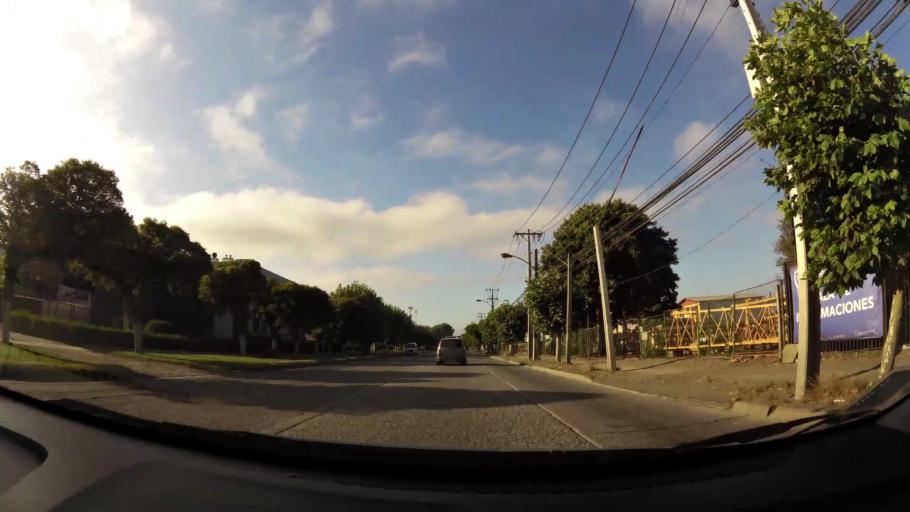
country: CL
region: Biobio
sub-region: Provincia de Concepcion
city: Concepcion
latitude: -36.7895
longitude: -73.0866
